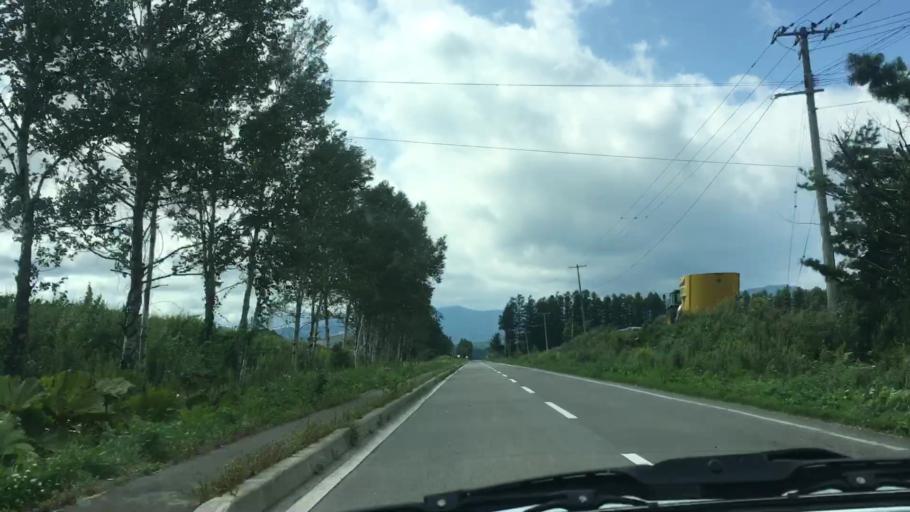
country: JP
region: Hokkaido
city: Otofuke
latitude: 43.2812
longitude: 143.3315
